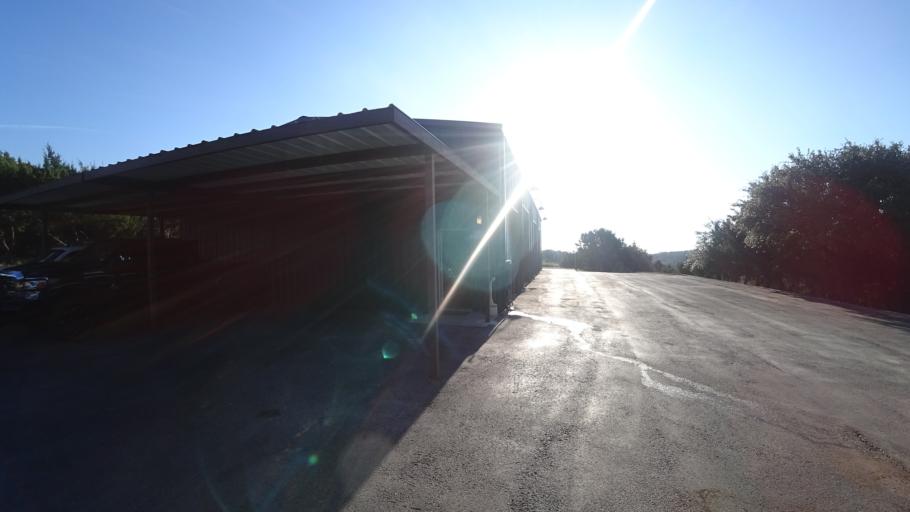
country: US
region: Texas
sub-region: Travis County
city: Hudson Bend
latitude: 30.3698
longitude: -97.8861
